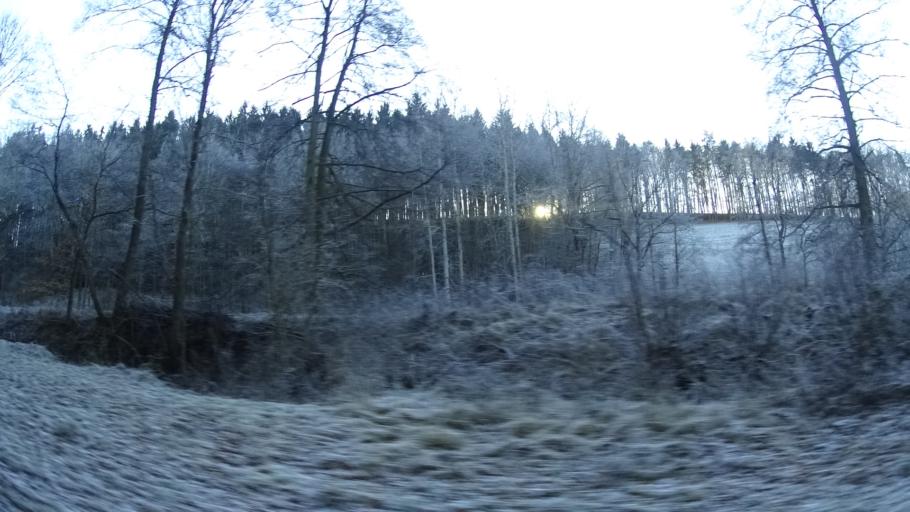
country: DE
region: Thuringia
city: Kleineutersdorf
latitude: 50.7864
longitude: 11.5878
